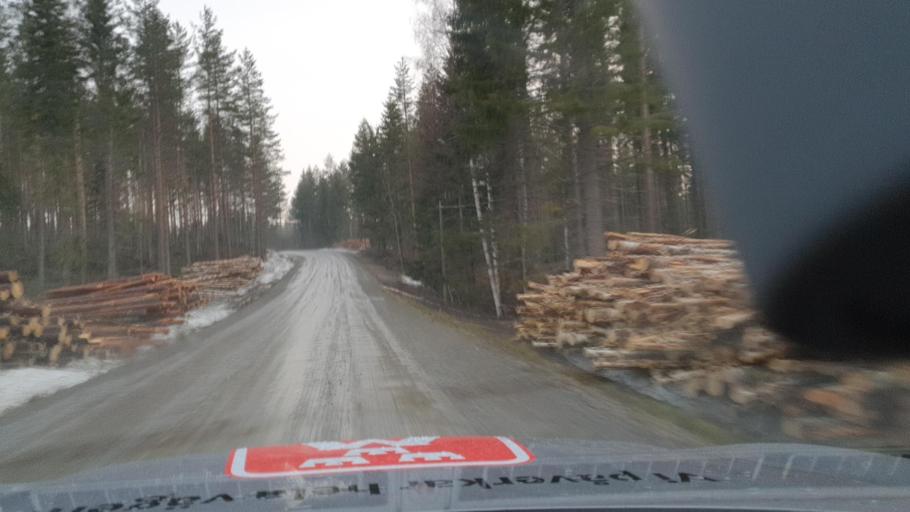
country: SE
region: Vaesternorrland
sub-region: OErnskoeldsviks Kommun
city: Bjasta
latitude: 63.2117
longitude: 18.3410
